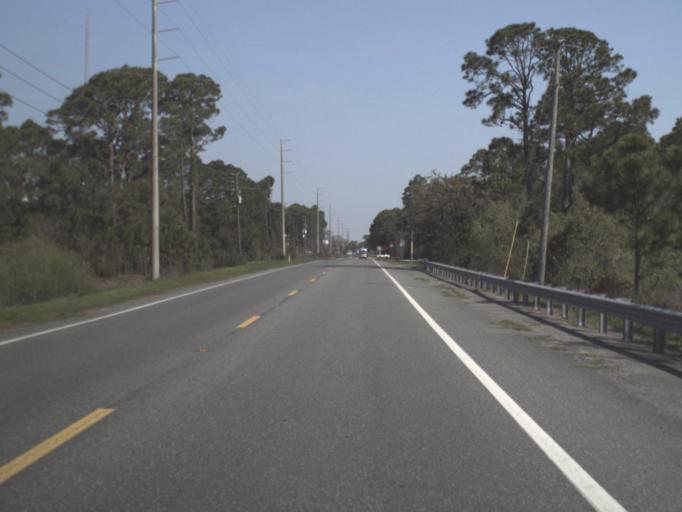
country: US
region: Florida
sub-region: Franklin County
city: Eastpoint
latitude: 29.7273
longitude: -84.8879
